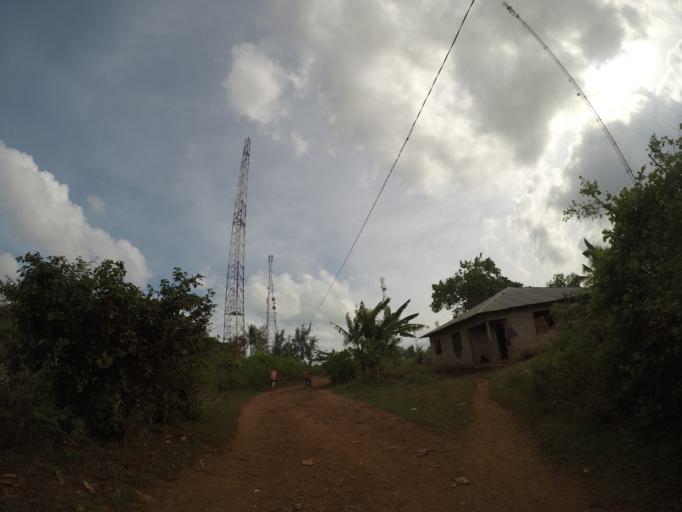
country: TZ
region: Zanzibar Central/South
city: Koani
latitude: -6.2229
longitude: 39.3191
